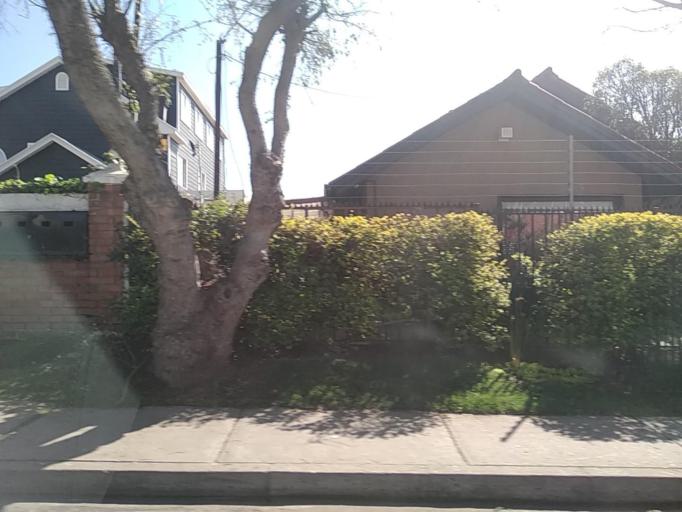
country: CL
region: Valparaiso
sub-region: Provincia de Valparaiso
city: Vina del Mar
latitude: -32.9396
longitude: -71.5429
